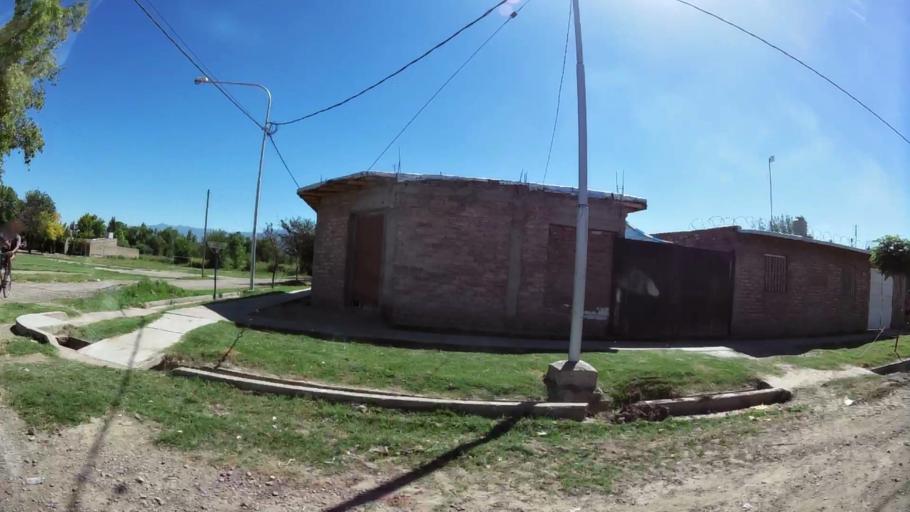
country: AR
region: Mendoza
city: Las Heras
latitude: -32.8252
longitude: -68.8258
